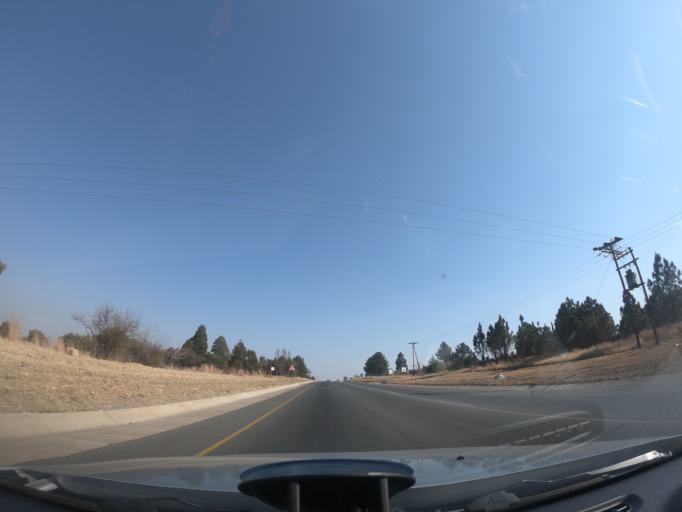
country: ZA
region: Gauteng
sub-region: City of Johannesburg Metropolitan Municipality
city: Diepsloot
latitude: -25.8692
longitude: 28.0308
